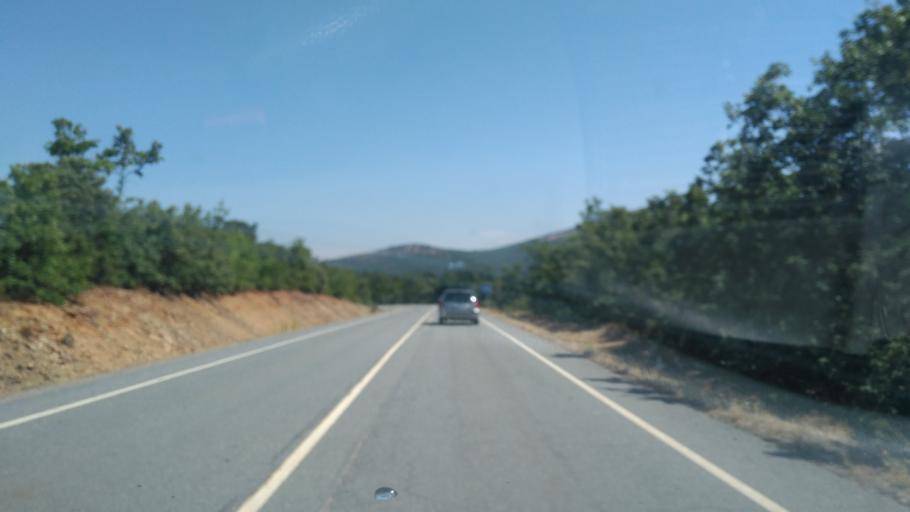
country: ES
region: Castille and Leon
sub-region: Provincia de Salamanca
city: Aldeanueva de la Sierra
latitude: 40.6014
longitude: -6.0930
